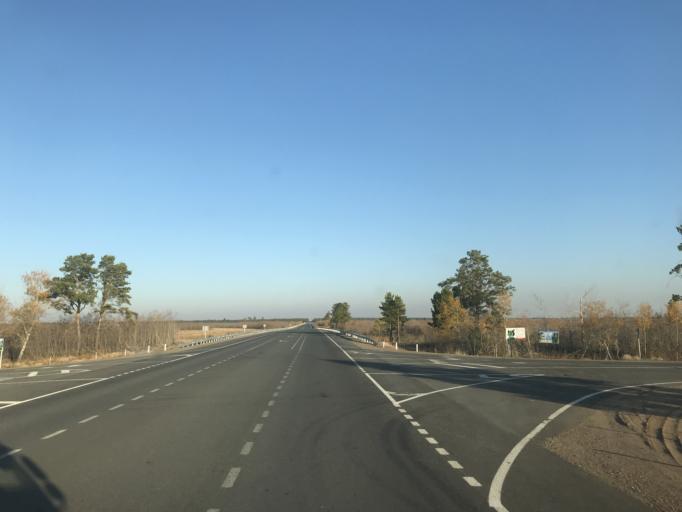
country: KZ
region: Pavlodar
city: Kurchatov
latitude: 51.1029
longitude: 78.9957
